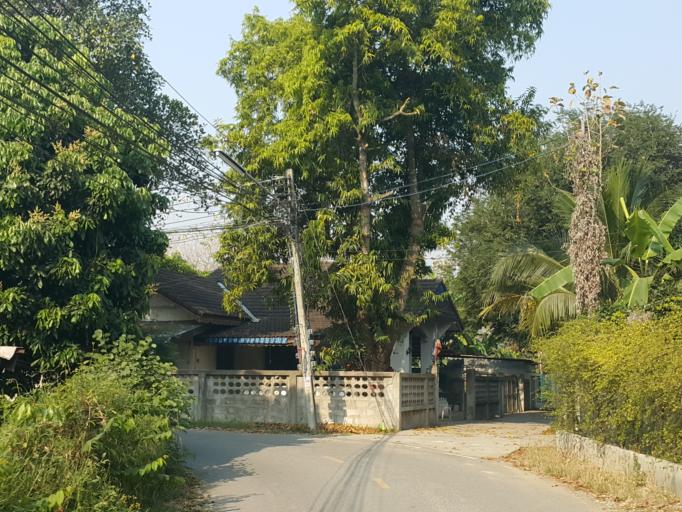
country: TH
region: Chiang Mai
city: San Kamphaeng
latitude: 18.7842
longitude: 99.0800
